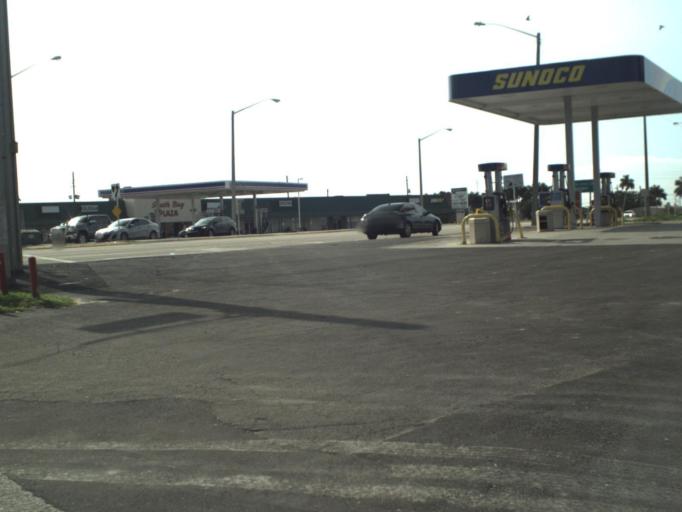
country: US
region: Florida
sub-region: Palm Beach County
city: South Bay
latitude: 26.6640
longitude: -80.7164
